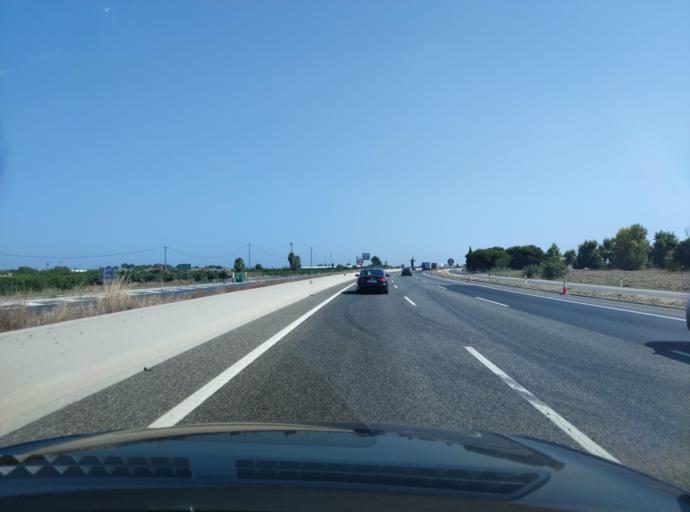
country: ES
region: Valencia
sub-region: Provincia de Valencia
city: Alginet
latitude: 39.2770
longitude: -0.4599
